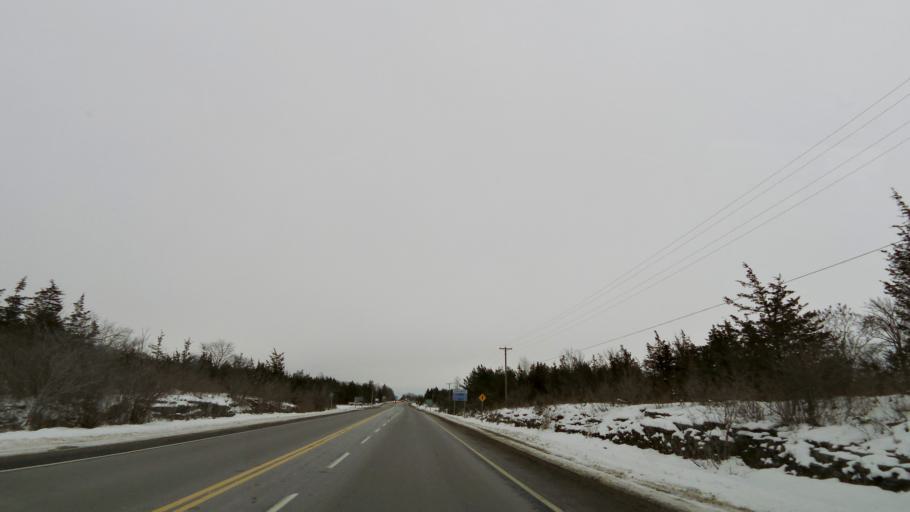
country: CA
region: Ontario
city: Ancaster
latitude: 43.3053
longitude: -80.1404
